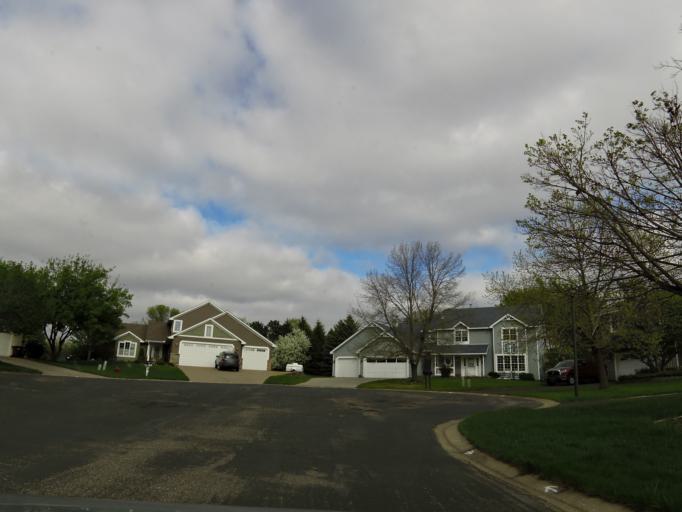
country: US
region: Minnesota
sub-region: Washington County
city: Woodbury
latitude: 44.9244
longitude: -92.9168
